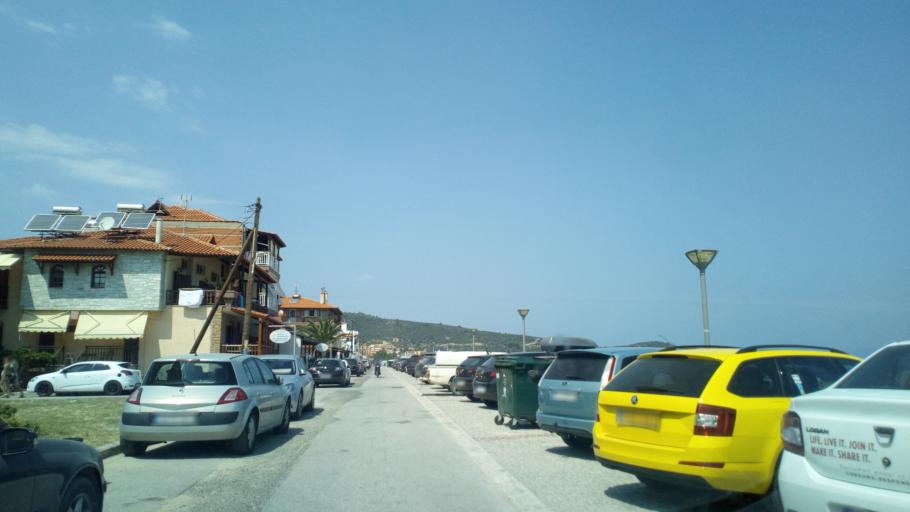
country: GR
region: Central Macedonia
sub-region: Nomos Chalkidikis
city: Sarti
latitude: 40.0898
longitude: 23.9789
